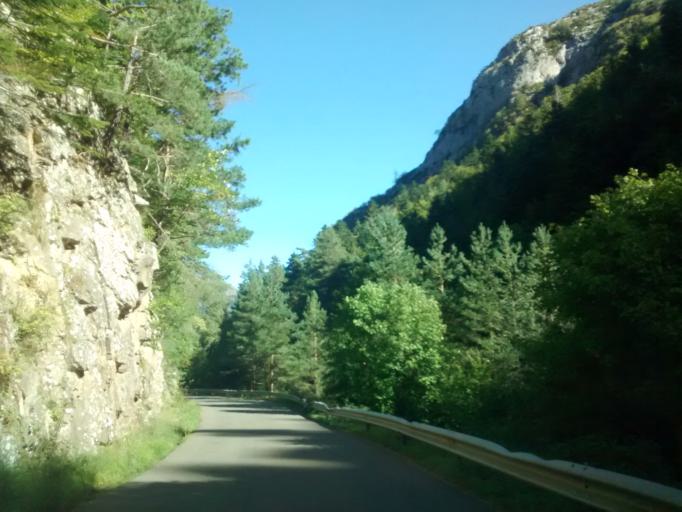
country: ES
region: Aragon
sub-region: Provincia de Huesca
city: Aragues del Puerto
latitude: 42.8179
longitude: -0.7113
